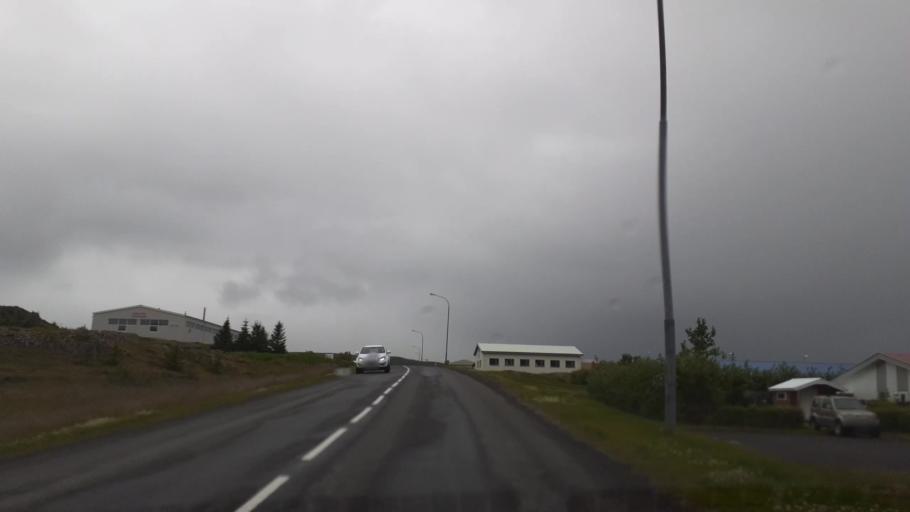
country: IS
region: East
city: Egilsstadir
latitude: 65.7529
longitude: -14.8358
